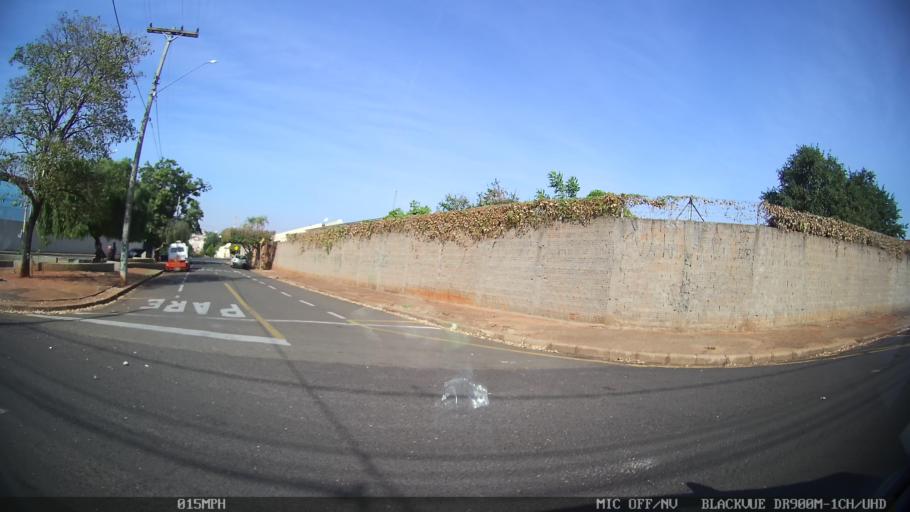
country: BR
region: Sao Paulo
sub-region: Sao Jose Do Rio Preto
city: Sao Jose do Rio Preto
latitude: -20.7927
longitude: -49.3812
